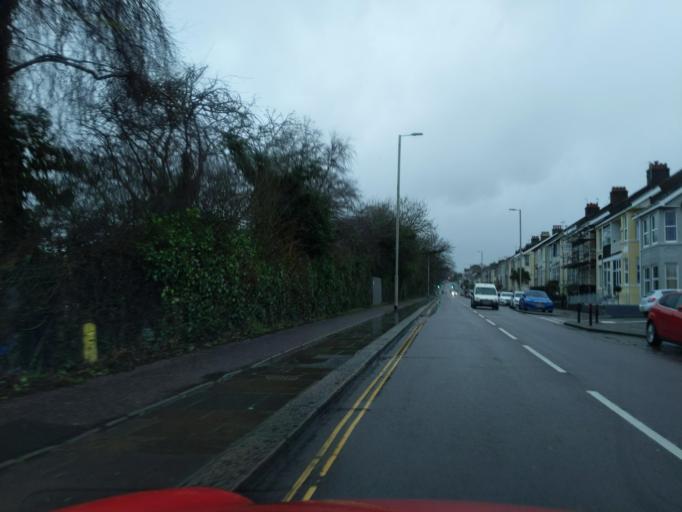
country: GB
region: England
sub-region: Plymouth
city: Plymouth
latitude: 50.3907
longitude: -4.1427
